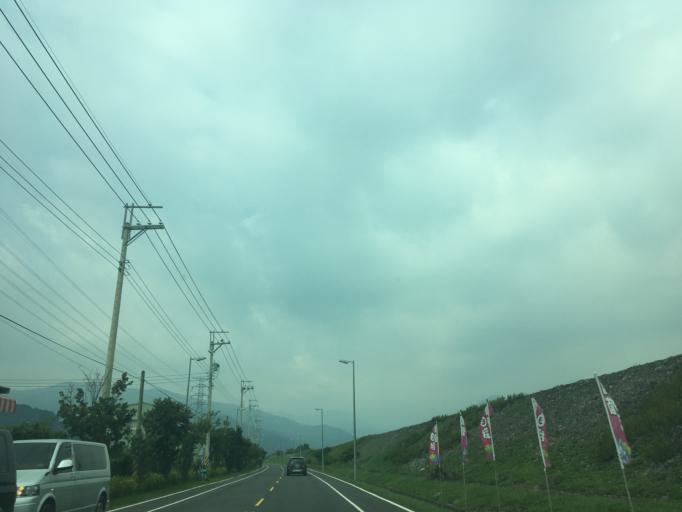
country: TW
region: Taiwan
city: Fengyuan
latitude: 24.2900
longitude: 120.8569
